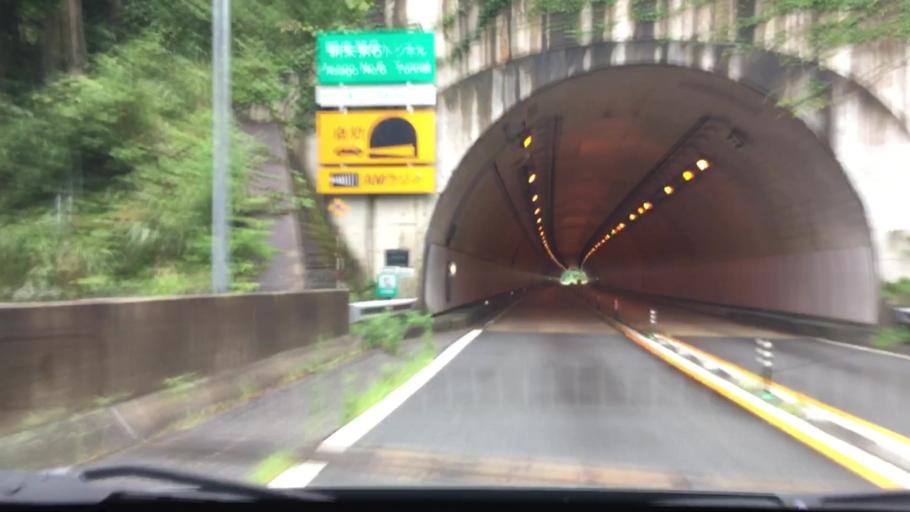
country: JP
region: Hyogo
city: Toyooka
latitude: 35.2413
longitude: 134.7873
